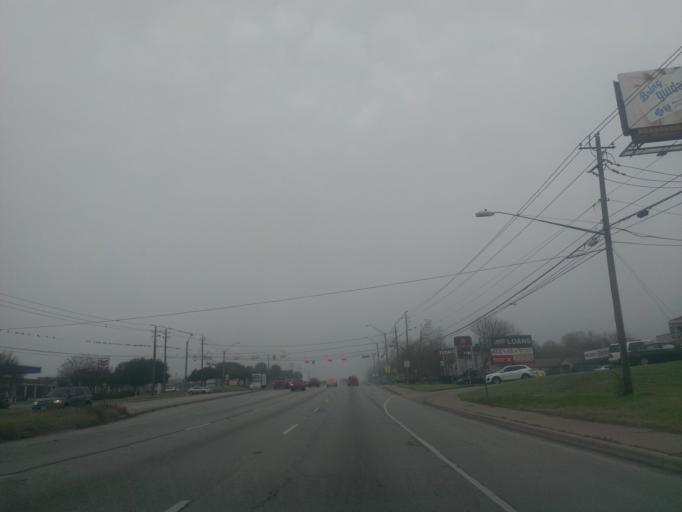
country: US
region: Texas
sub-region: Travis County
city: Wells Branch
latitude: 30.4153
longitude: -97.6946
